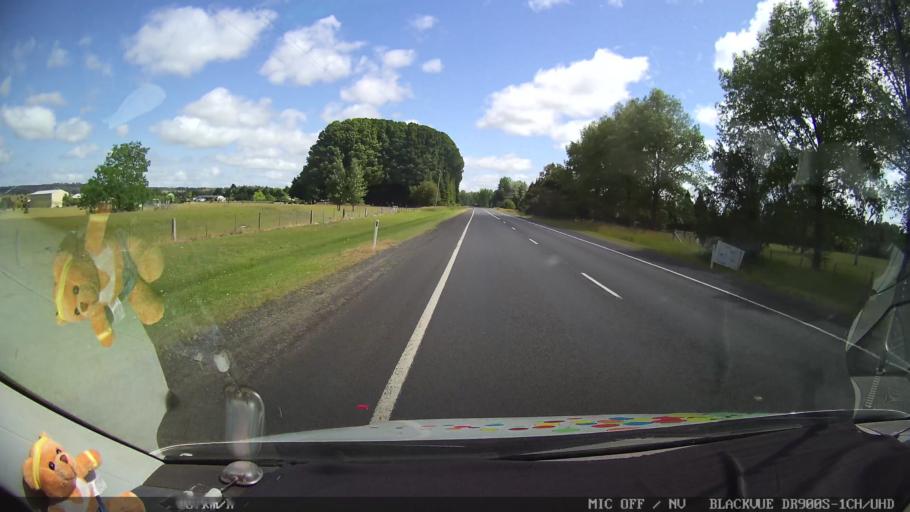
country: AU
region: New South Wales
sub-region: Glen Innes Severn
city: Glen Innes
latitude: -29.8161
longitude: 151.7410
